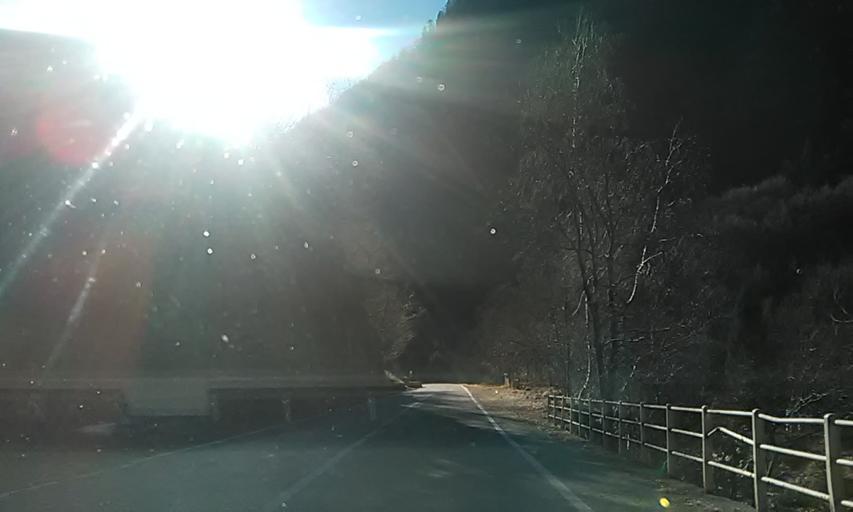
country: IT
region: Piedmont
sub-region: Provincia di Vercelli
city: Rimasco
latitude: 45.8799
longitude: 8.0671
